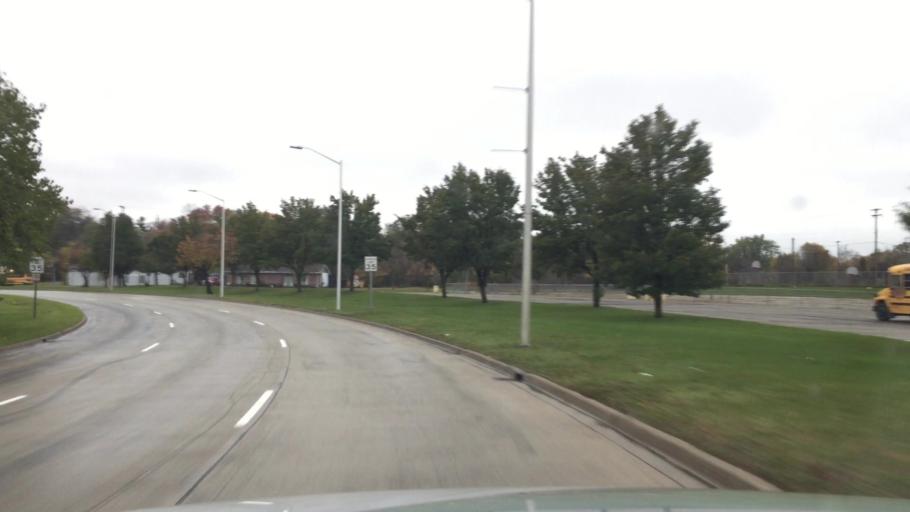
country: US
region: Michigan
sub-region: Oakland County
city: Pontiac
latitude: 42.6421
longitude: -83.2977
